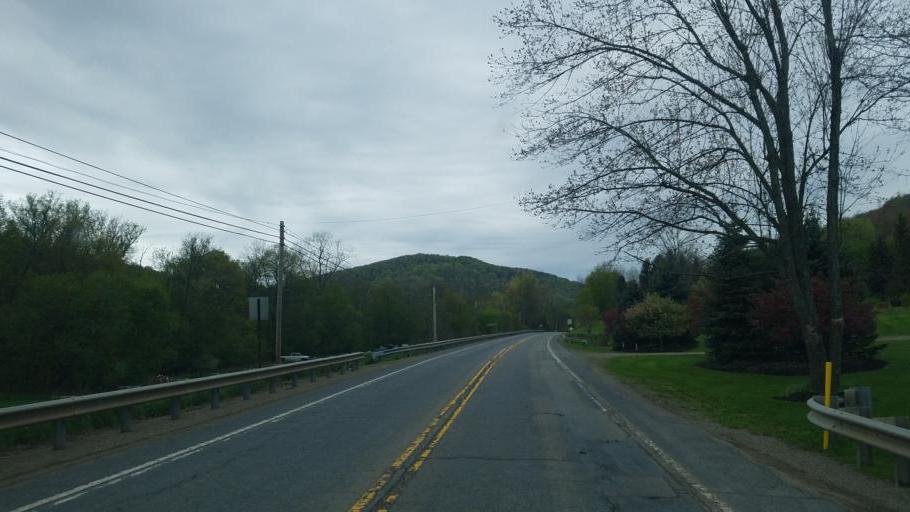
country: US
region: Pennsylvania
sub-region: Tioga County
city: Westfield
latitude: 41.9146
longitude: -77.6100
